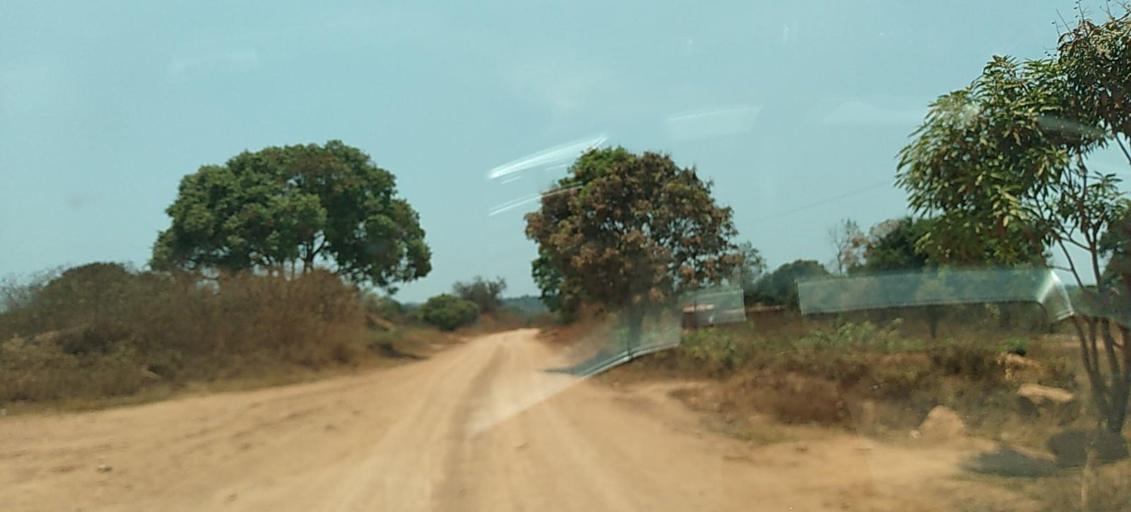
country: CD
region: Katanga
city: Kipushi
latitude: -11.7803
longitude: 27.1878
